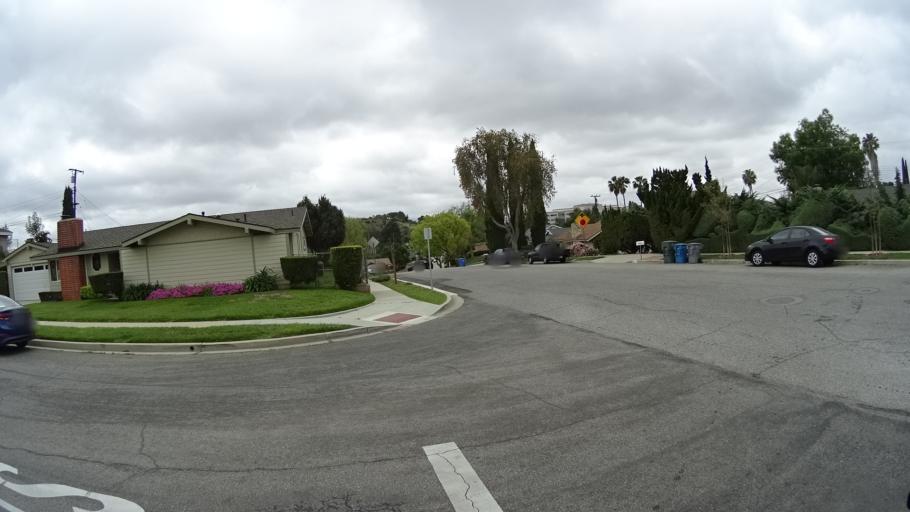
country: US
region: California
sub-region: Ventura County
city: Thousand Oaks
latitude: 34.2101
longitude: -118.8785
